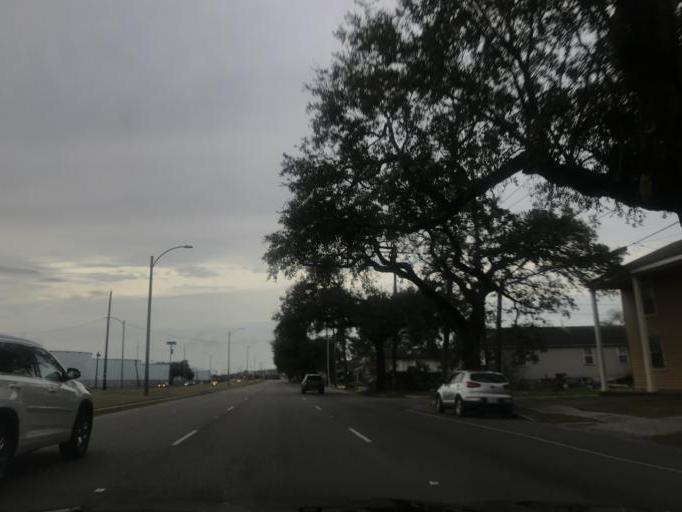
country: US
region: Louisiana
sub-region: Jefferson Parish
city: Jefferson
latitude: 29.9612
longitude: -90.1268
